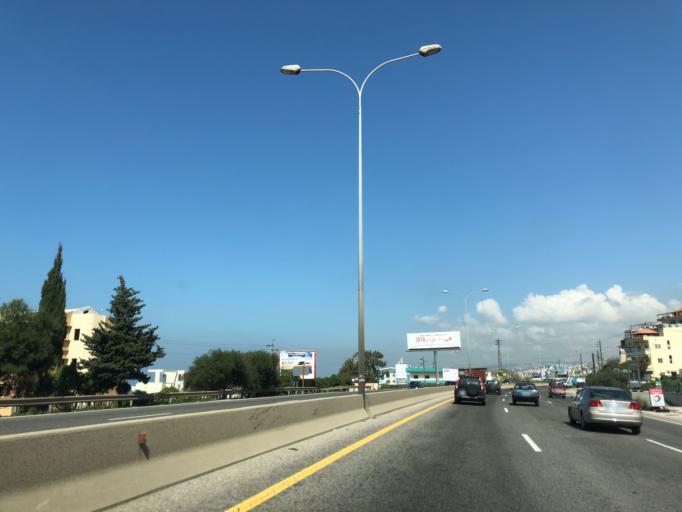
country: LB
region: Mont-Liban
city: Jbail
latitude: 34.0703
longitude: 35.6439
